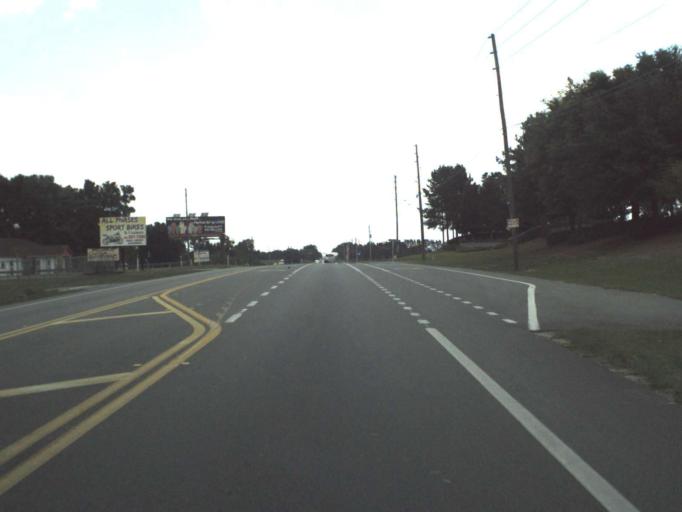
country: US
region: Florida
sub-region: Marion County
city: Belleview
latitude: 29.0807
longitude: -82.0535
